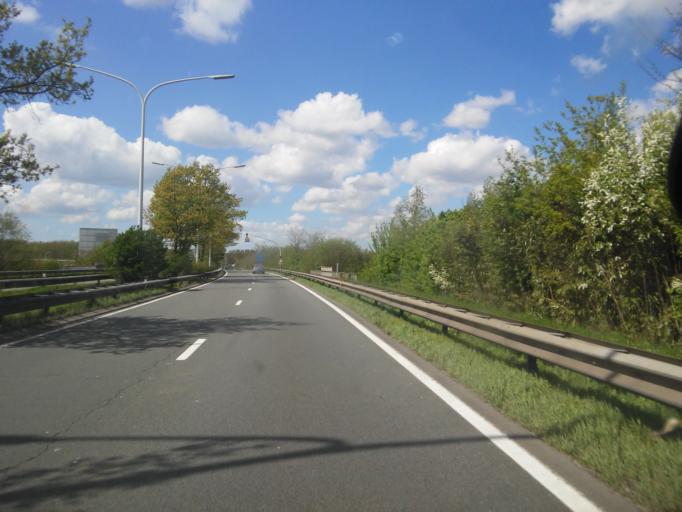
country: BE
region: Flanders
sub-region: Provincie Antwerpen
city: Puurs
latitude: 51.0761
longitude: 4.3015
